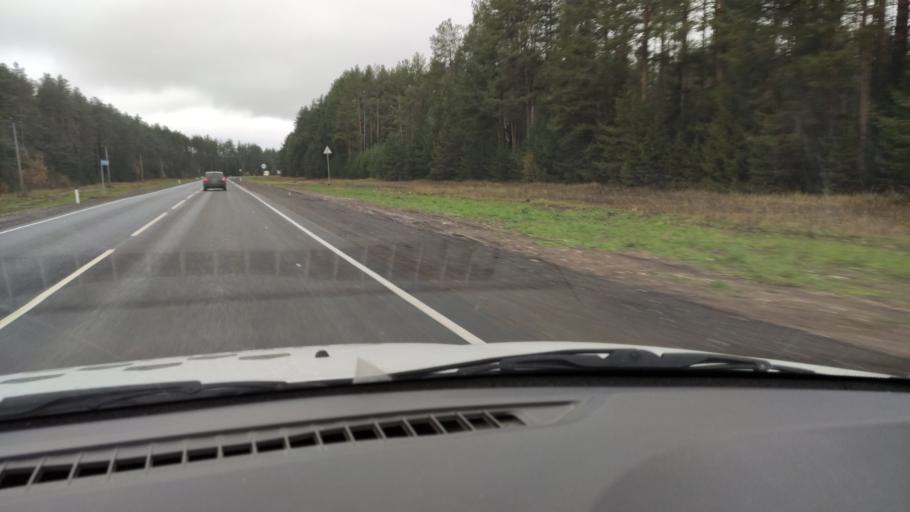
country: RU
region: Kirov
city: Belaya Kholunitsa
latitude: 58.8429
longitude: 50.8056
